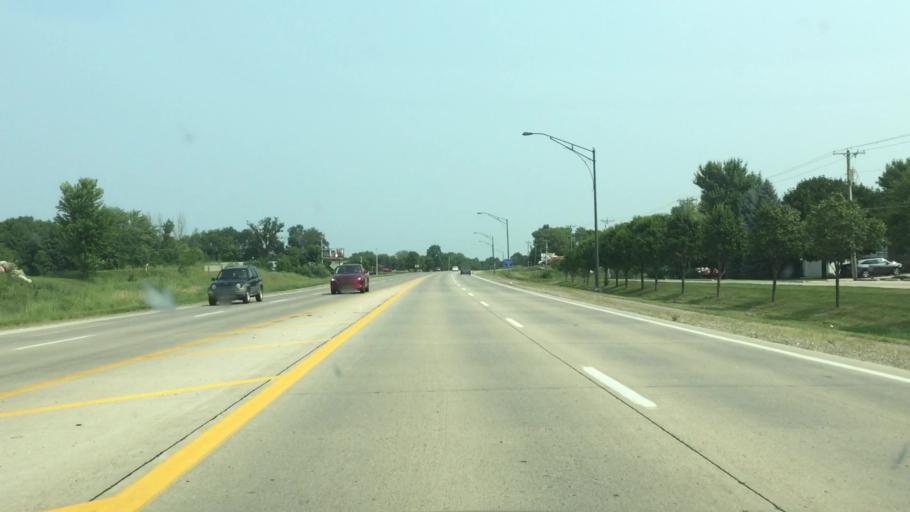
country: US
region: Iowa
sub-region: Dickinson County
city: Arnolds Park
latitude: 43.3549
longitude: -95.1421
